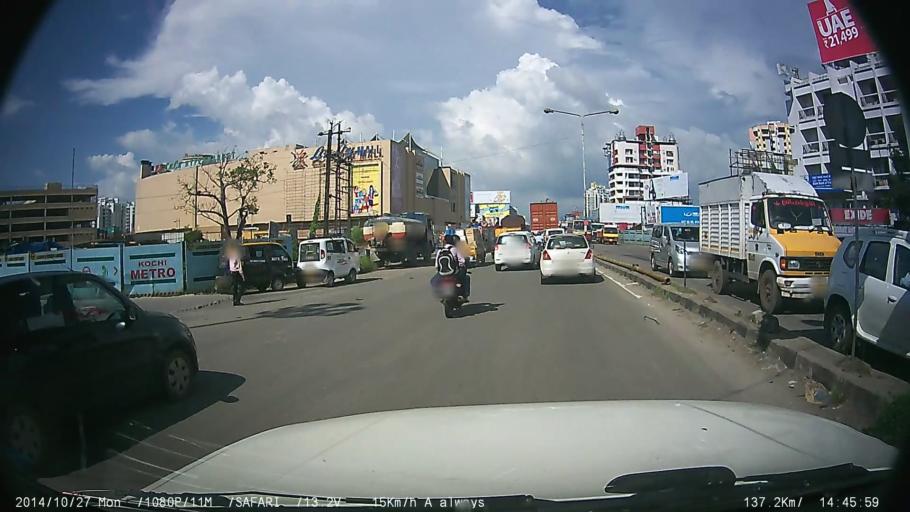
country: IN
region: Kerala
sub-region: Ernakulam
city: Elur
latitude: 10.0246
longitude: 76.3082
